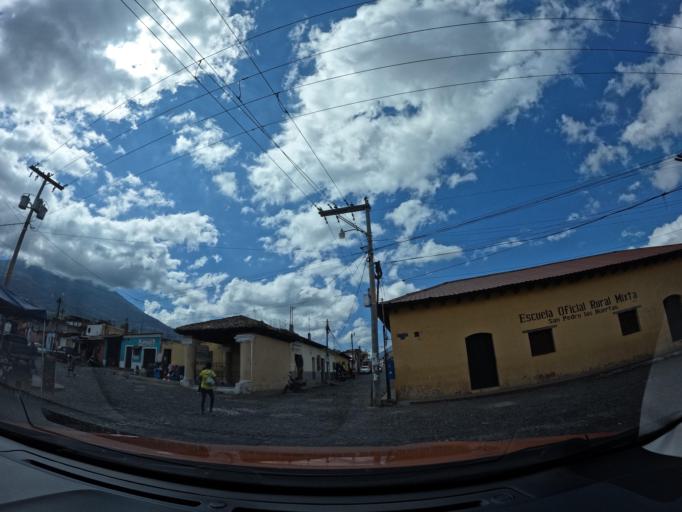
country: GT
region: Sacatepequez
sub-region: Municipio de Santa Maria de Jesus
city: Santa Maria de Jesus
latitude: 14.5305
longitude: -90.7404
